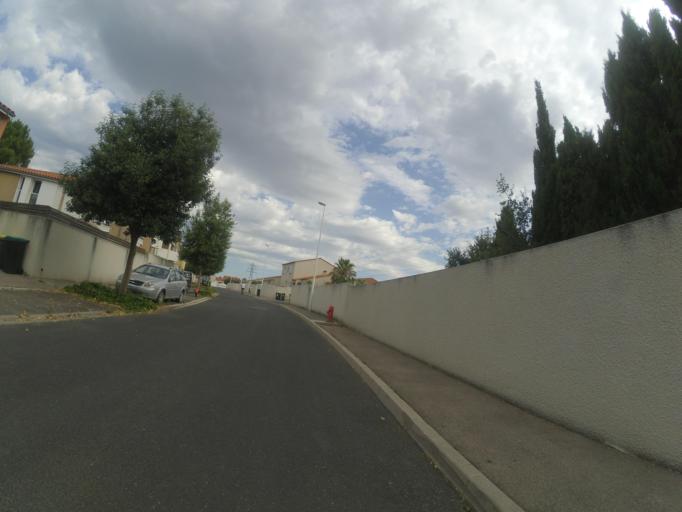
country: FR
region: Languedoc-Roussillon
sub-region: Departement des Pyrenees-Orientales
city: Toulouges
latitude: 42.6706
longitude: 2.8493
